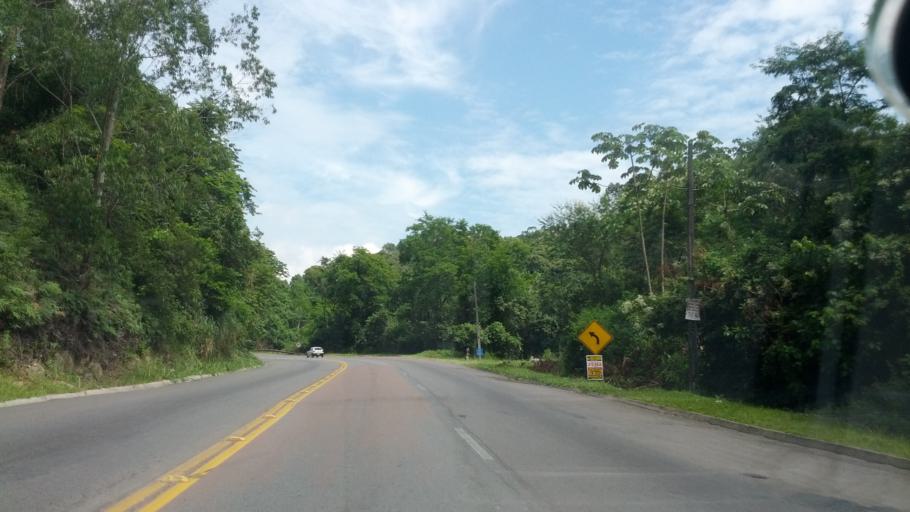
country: BR
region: Santa Catarina
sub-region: Ibirama
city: Ibirama
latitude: -27.0924
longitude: -49.5220
